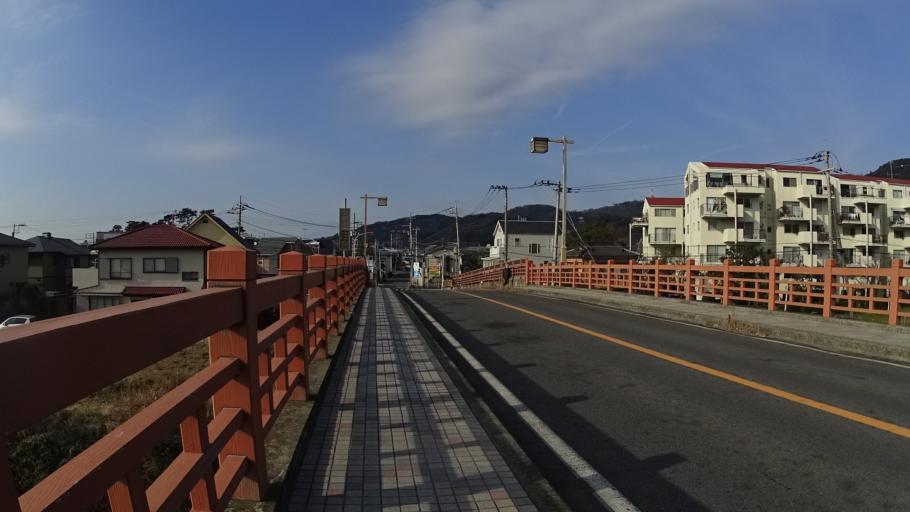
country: JP
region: Kanagawa
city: Hiratsuka
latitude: 35.3168
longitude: 139.3302
